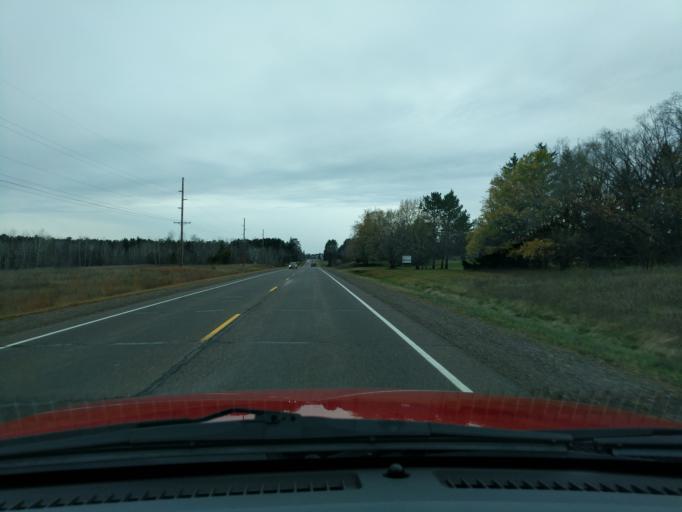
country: US
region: Wisconsin
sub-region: Washburn County
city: Spooner
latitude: 45.8219
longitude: -91.8740
